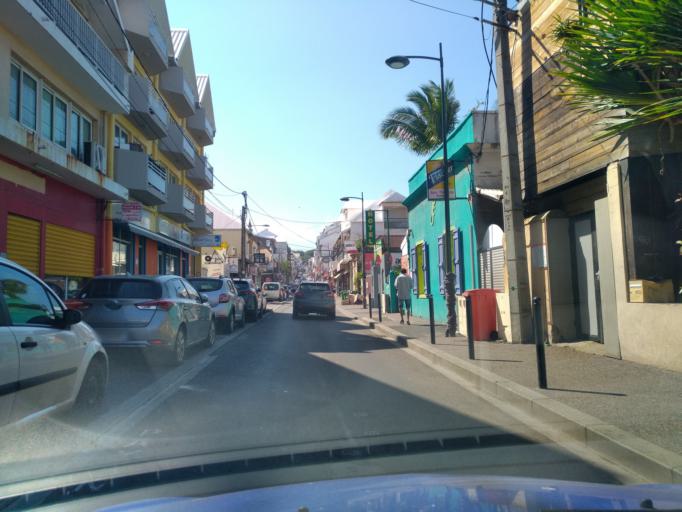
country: RE
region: Reunion
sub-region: Reunion
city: Saint-Pierre
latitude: -21.3431
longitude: 55.4744
